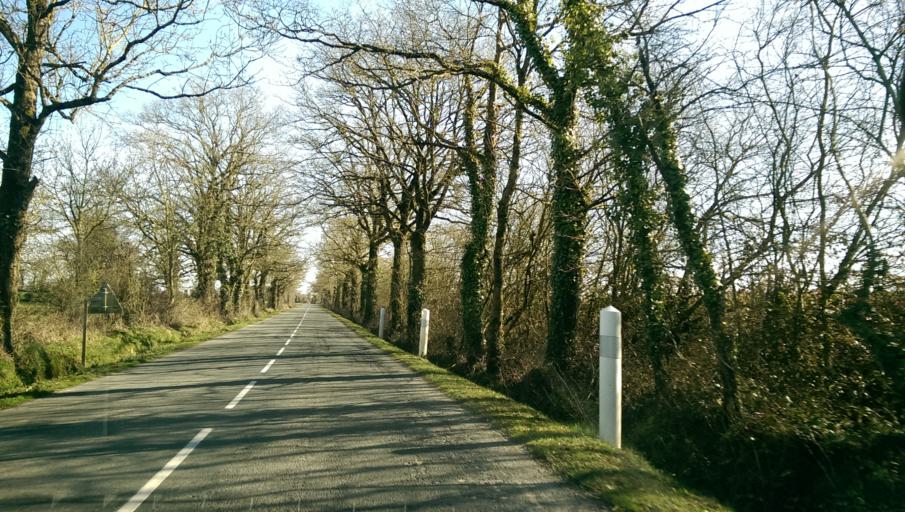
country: FR
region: Pays de la Loire
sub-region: Departement de la Vendee
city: Beaurepaire
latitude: 46.9278
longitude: -1.1095
